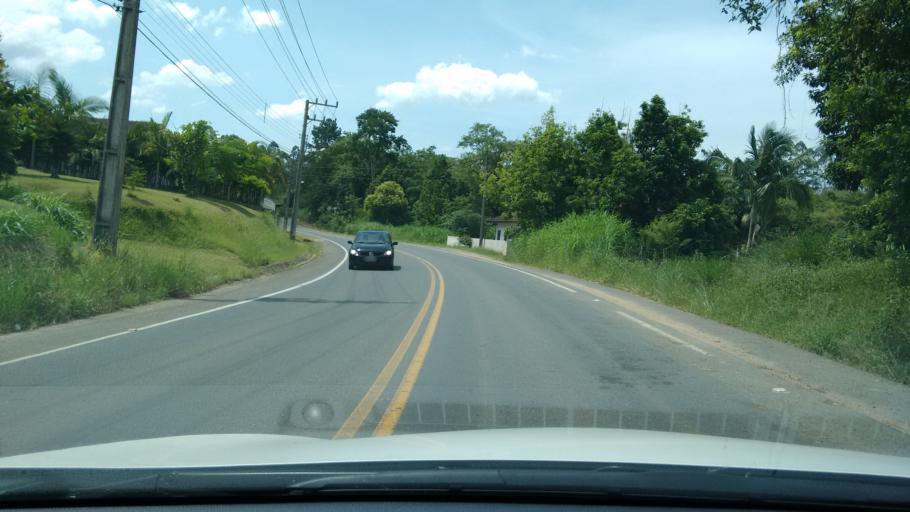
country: BR
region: Santa Catarina
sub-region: Timbo
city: Timbo
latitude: -26.8317
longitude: -49.3212
